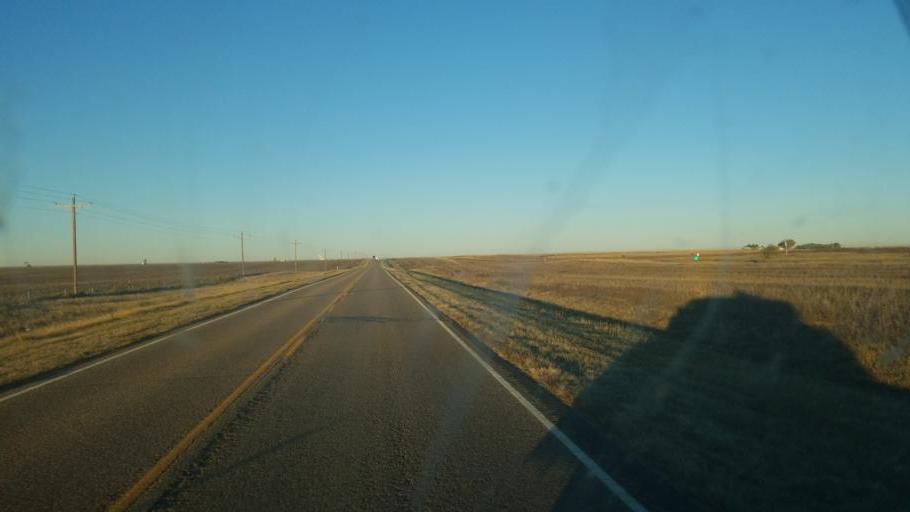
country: US
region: Colorado
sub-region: Cheyenne County
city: Cheyenne Wells
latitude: 38.8481
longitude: -102.1103
